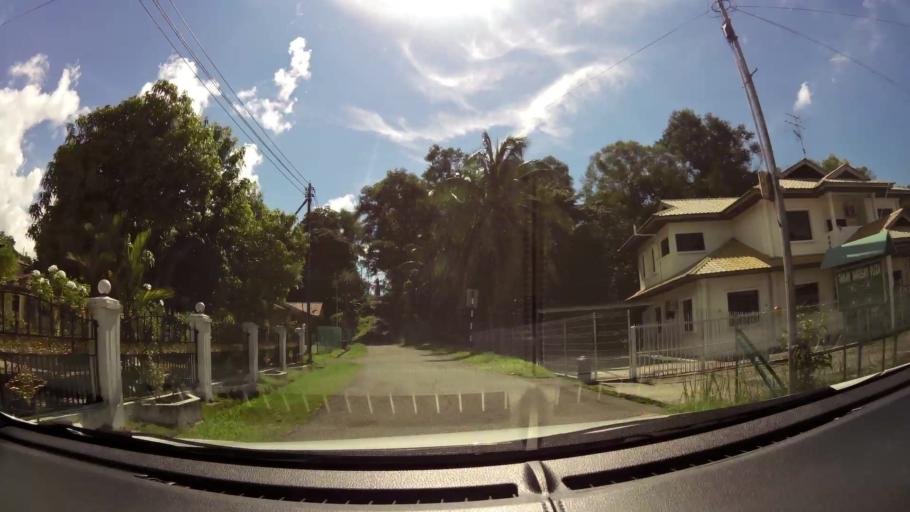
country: BN
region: Brunei and Muara
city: Bandar Seri Begawan
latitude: 4.9626
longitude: 114.9444
